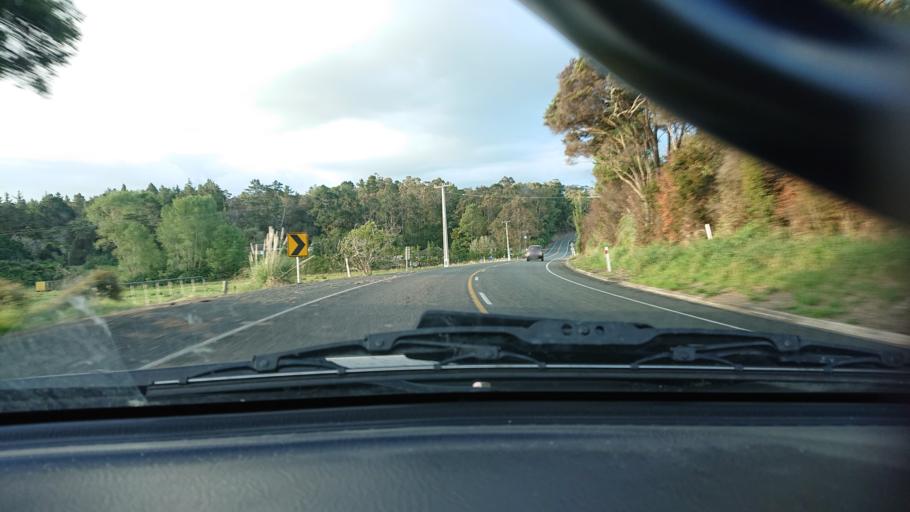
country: NZ
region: Auckland
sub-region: Auckland
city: Parakai
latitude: -36.5303
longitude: 174.4545
